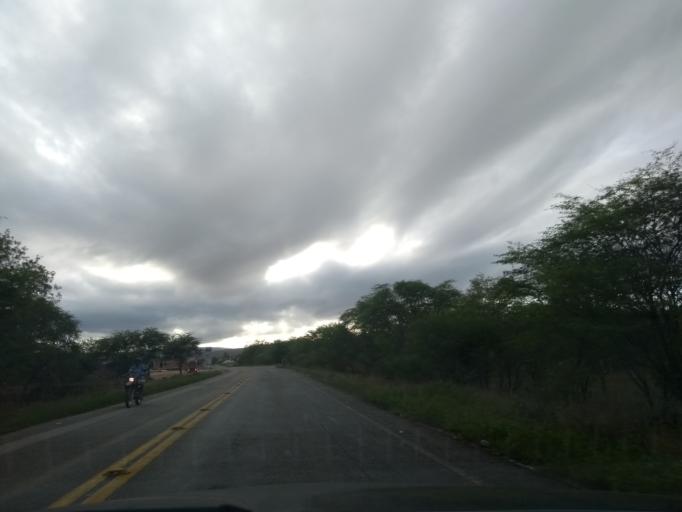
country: BR
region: Bahia
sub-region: Ituacu
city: Ituacu
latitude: -13.7661
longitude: -41.0401
